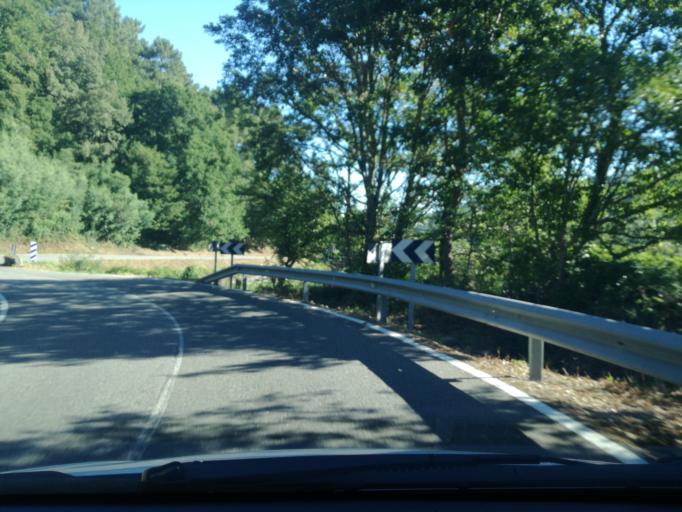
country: ES
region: Galicia
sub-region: Provincia de Ourense
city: Lobios
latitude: 41.8620
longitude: -8.1082
